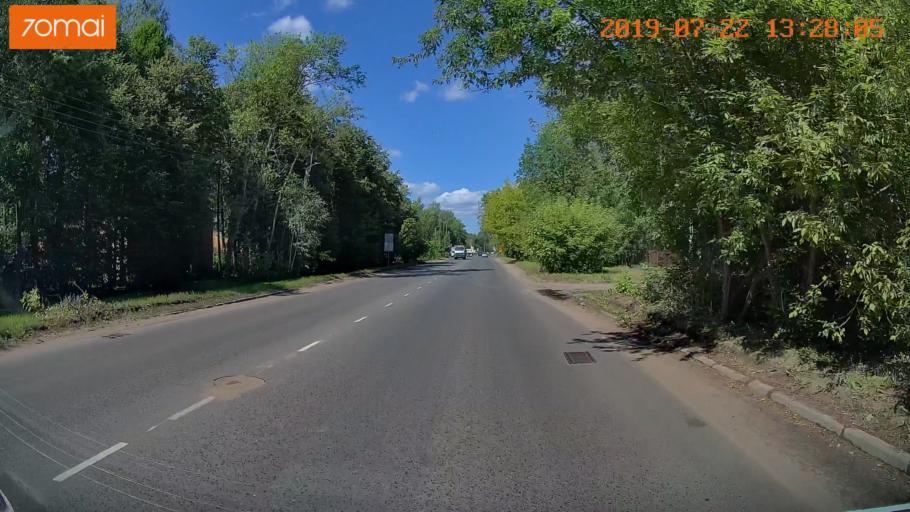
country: RU
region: Ivanovo
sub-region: Gorod Ivanovo
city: Ivanovo
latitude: 57.0394
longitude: 40.9495
